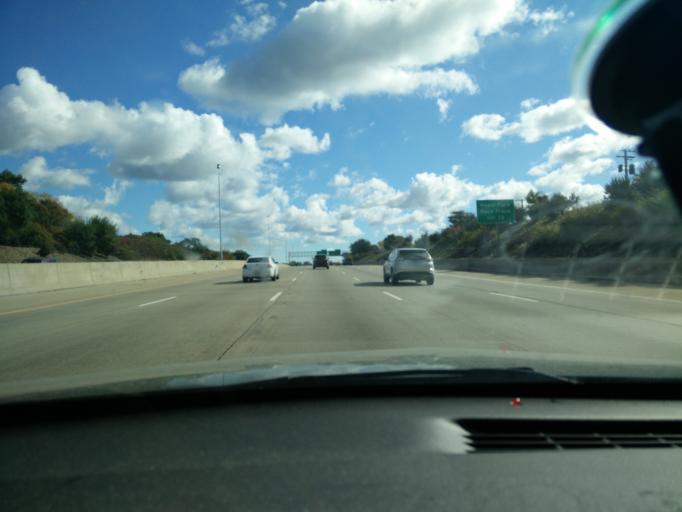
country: US
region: Michigan
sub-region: Oakland County
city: Madison Heights
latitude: 42.4770
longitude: -83.1033
